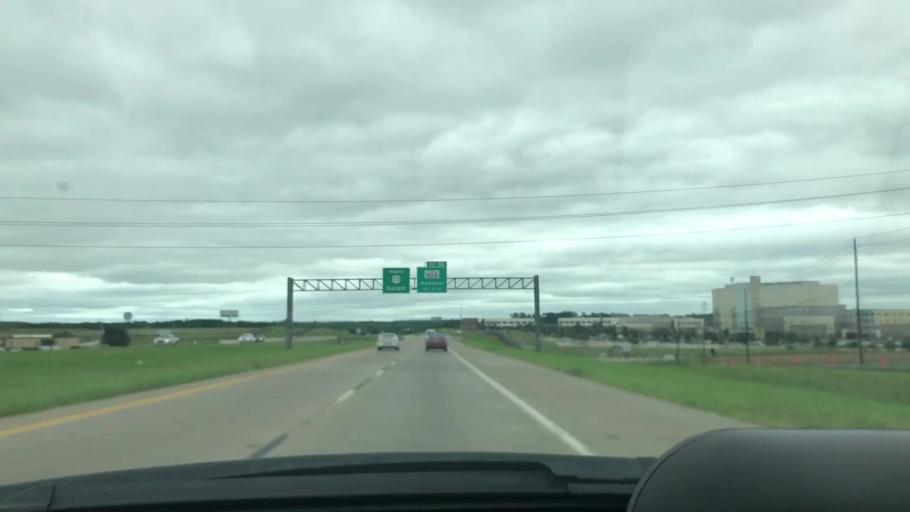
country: US
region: Texas
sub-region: Grayson County
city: Sherman
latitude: 33.7059
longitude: -96.5910
